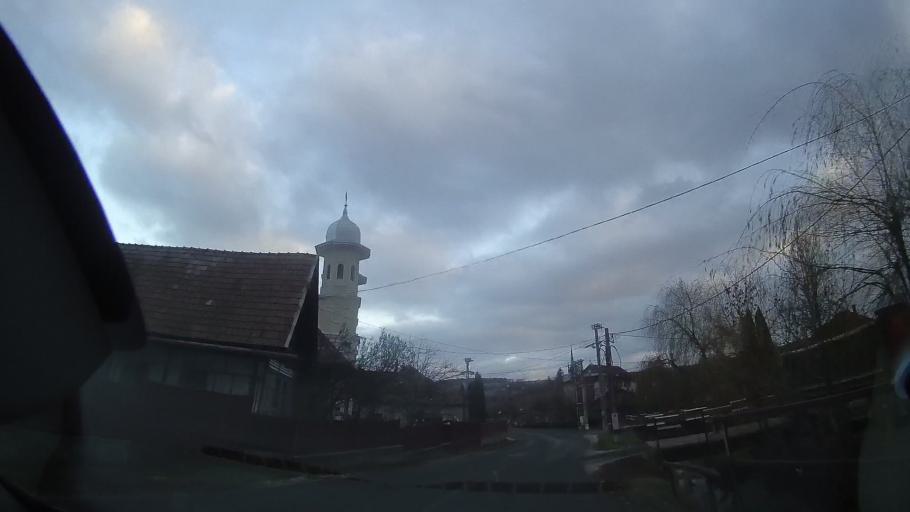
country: RO
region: Cluj
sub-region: Comuna Manastireni
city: Manastireni
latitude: 46.7814
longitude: 23.0841
